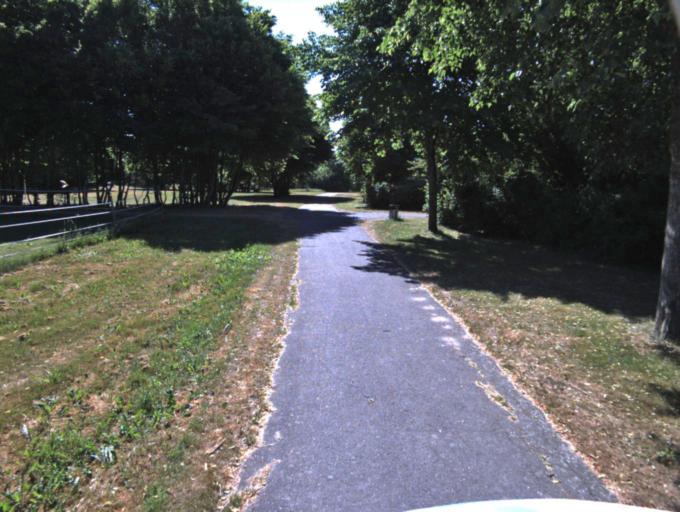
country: SE
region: Skane
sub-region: Ostra Goinge Kommun
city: Hanaskog
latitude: 56.0791
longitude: 14.0937
